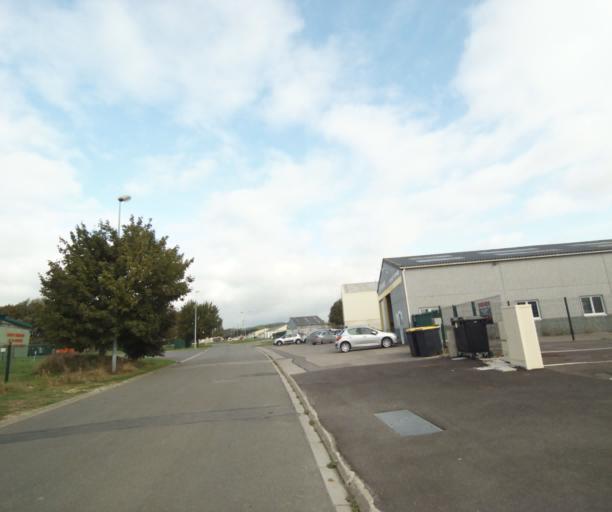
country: FR
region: Nord-Pas-de-Calais
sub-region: Departement du Pas-de-Calais
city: Etaples
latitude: 50.5162
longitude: 1.6657
